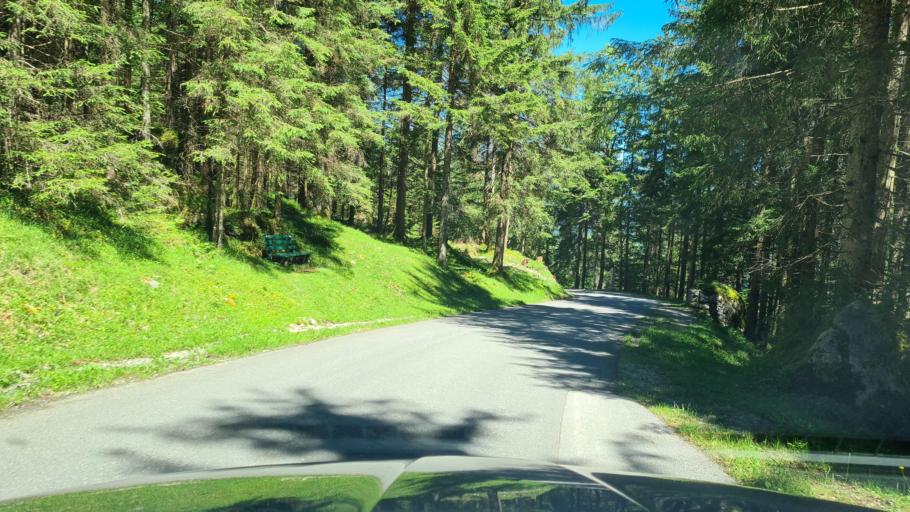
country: AT
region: Salzburg
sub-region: Politischer Bezirk Zell am See
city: Sankt Martin bei Lofer
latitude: 47.5609
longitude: 12.7014
